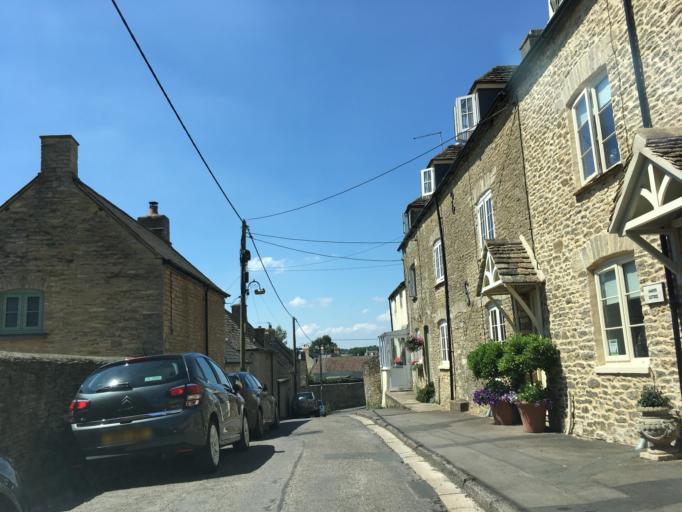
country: GB
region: England
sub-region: Gloucestershire
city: Tetbury
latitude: 51.6362
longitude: -2.1631
